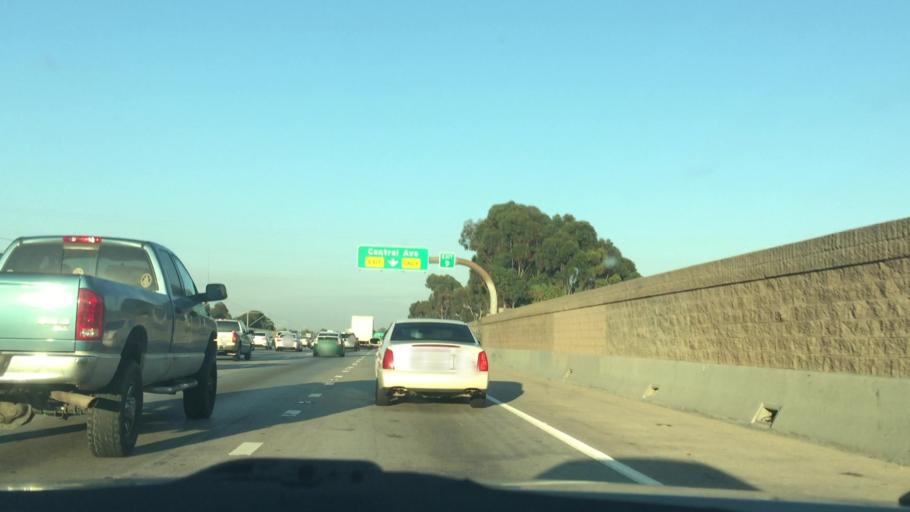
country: US
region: California
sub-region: Los Angeles County
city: Willowbrook
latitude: 33.9273
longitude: -118.2653
